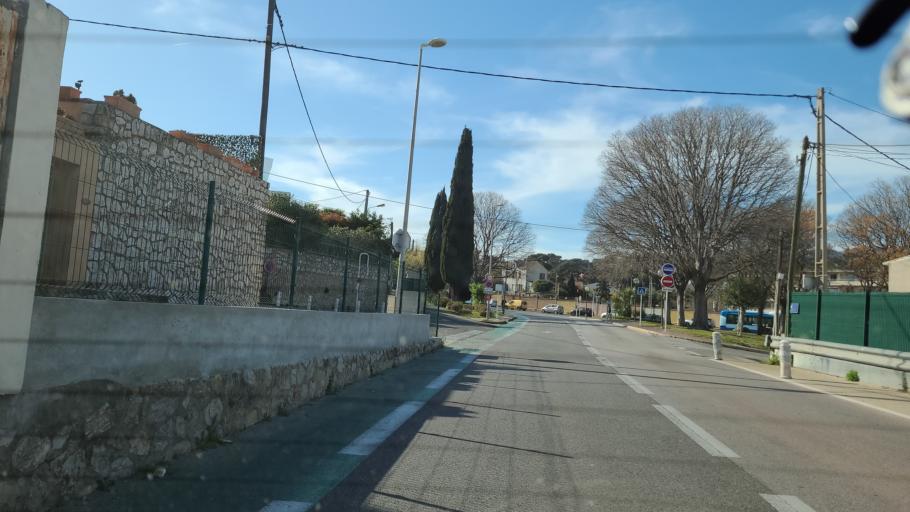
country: FR
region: Provence-Alpes-Cote d'Azur
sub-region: Departement du Var
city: La Seyne-sur-Mer
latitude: 43.1280
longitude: 5.8929
